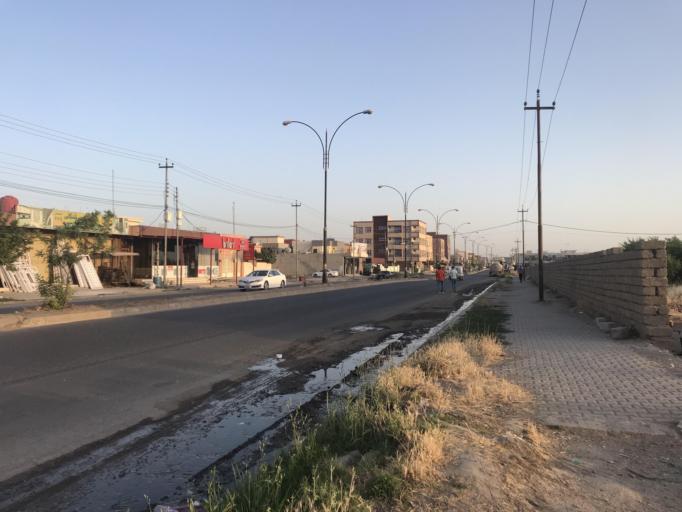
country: IQ
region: Dahuk
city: Saymayl
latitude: 36.8619
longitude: 42.8331
